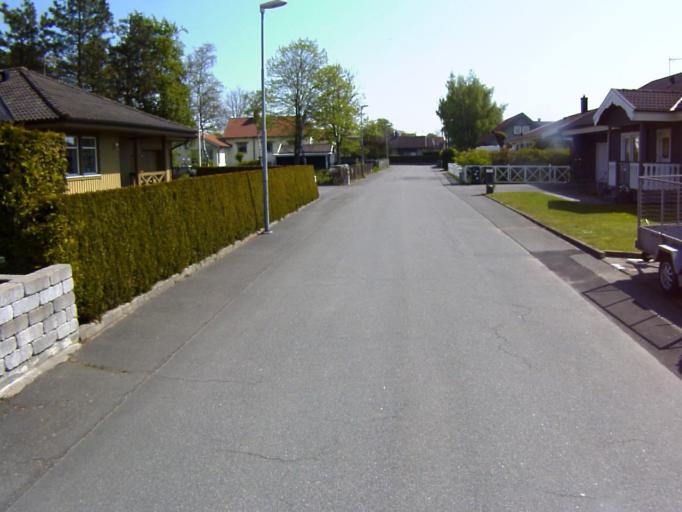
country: SE
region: Skane
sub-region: Kristianstads Kommun
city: Ahus
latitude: 55.9805
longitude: 14.2693
